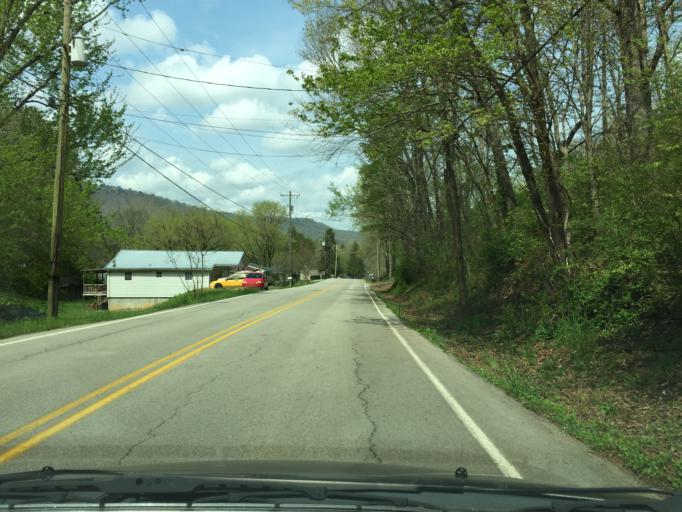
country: US
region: Tennessee
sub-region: Hamilton County
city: Walden
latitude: 35.1533
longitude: -85.2822
